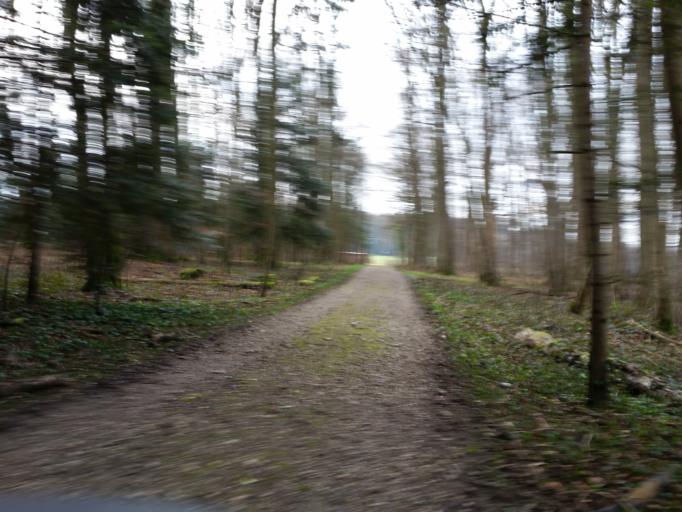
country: CH
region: Saint Gallen
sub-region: Wahlkreis St. Gallen
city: Muolen
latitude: 47.5494
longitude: 9.3306
